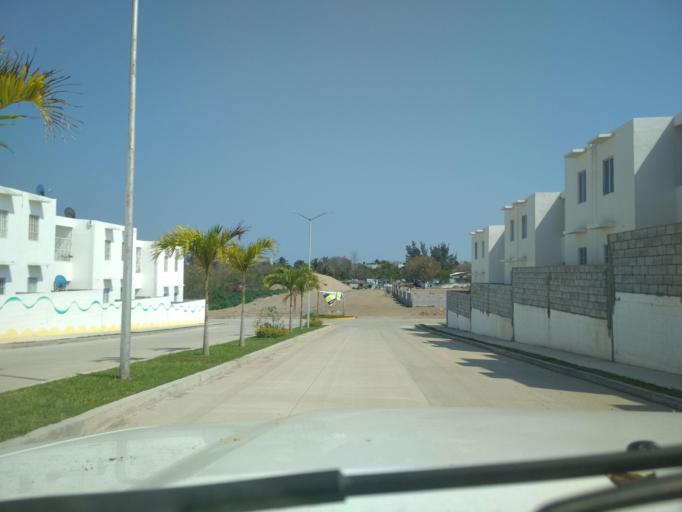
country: MX
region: Veracruz
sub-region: Veracruz
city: Rio Medio [Granja]
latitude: 19.2110
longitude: -96.2122
